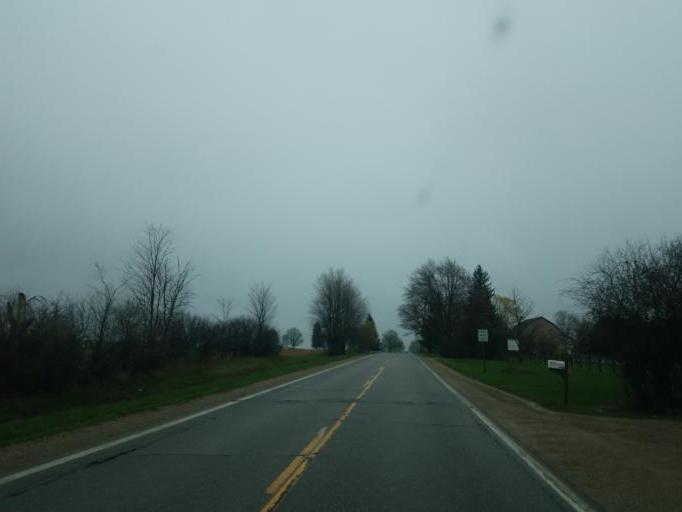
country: US
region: Michigan
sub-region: Isabella County
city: Shepherd
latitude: 43.5242
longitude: -84.7552
